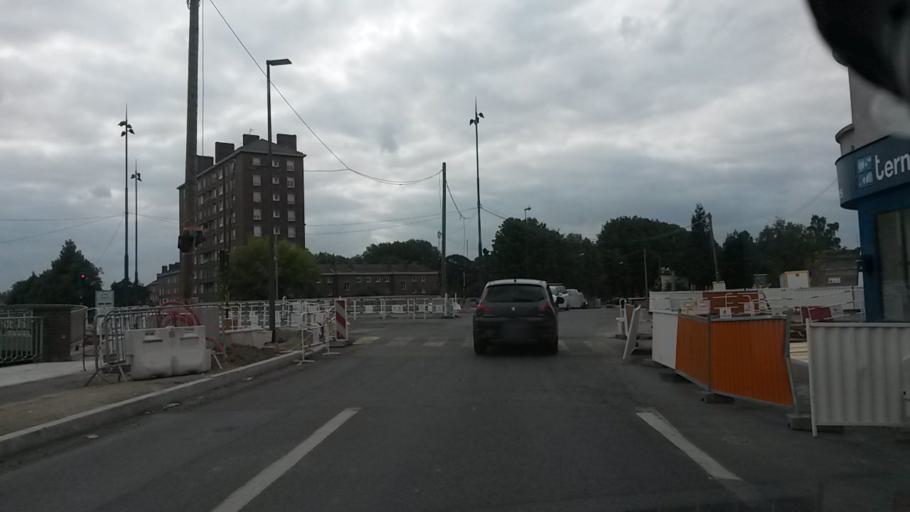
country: FR
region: Picardie
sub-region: Departement de la Somme
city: Amiens
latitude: 49.9021
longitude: 2.3004
